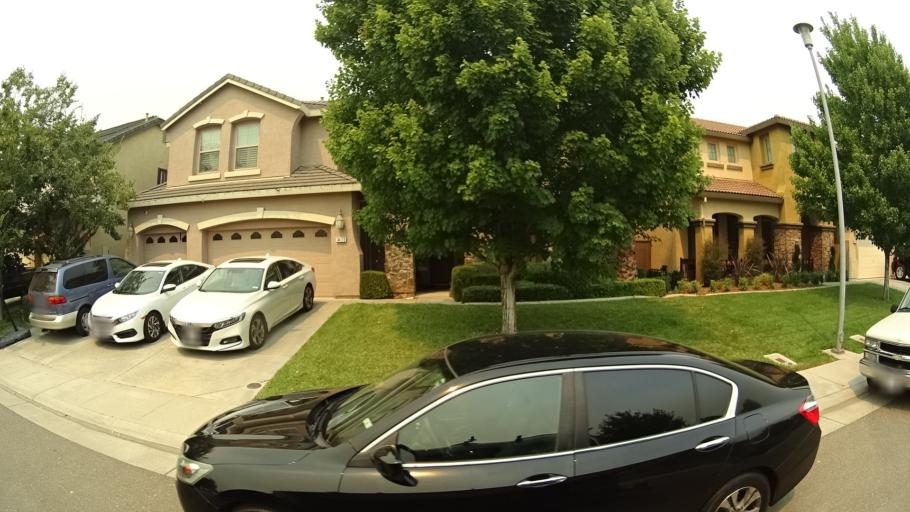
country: US
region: California
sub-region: Sacramento County
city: Laguna
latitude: 38.4034
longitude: -121.4204
